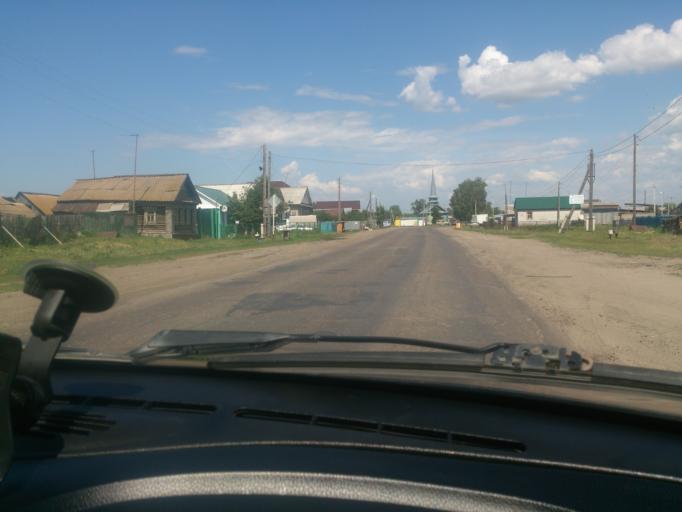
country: RU
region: Ulyanovsk
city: Cherdakly
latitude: 54.4288
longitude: 48.8955
